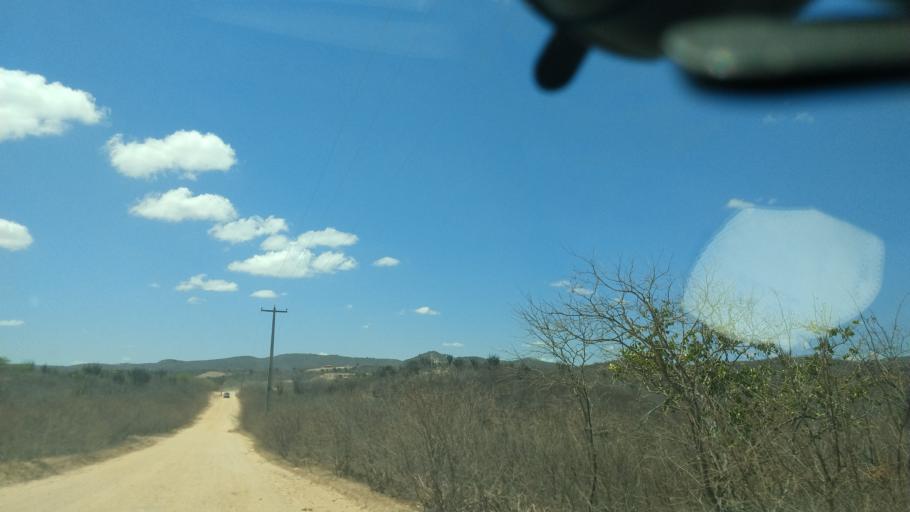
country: BR
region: Rio Grande do Norte
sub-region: Cerro Cora
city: Cerro Cora
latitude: -6.0110
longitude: -36.2941
